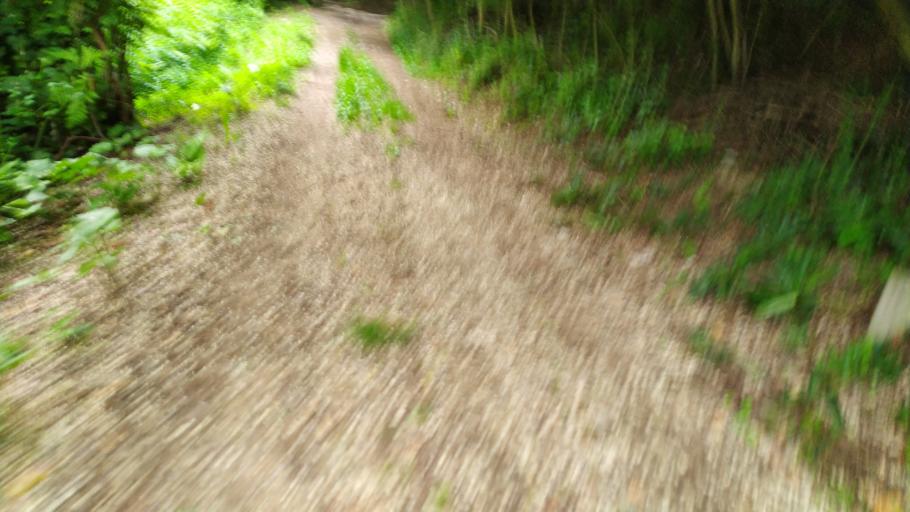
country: IT
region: Veneto
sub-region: Provincia di Vicenza
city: Torrebelvicino
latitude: 45.6900
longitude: 11.3113
